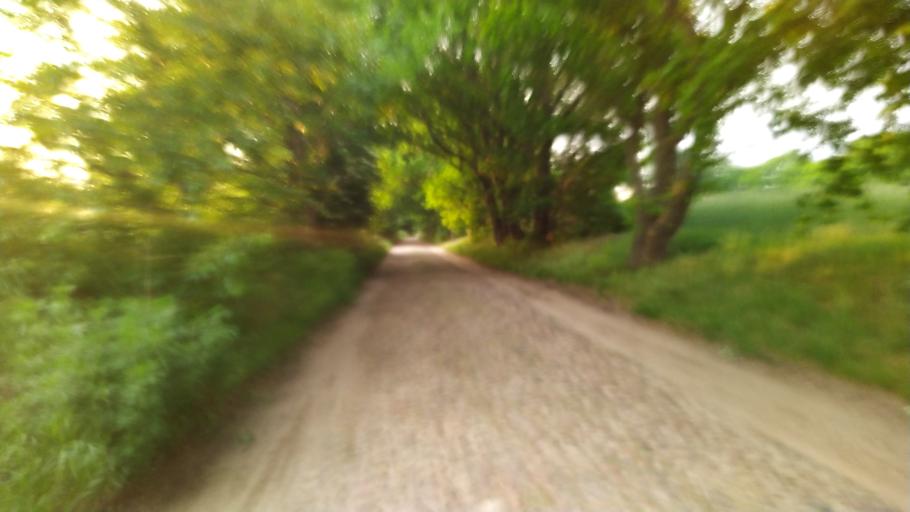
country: DE
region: Lower Saxony
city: Neu Wulmstorf
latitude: 53.4767
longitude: 9.8285
